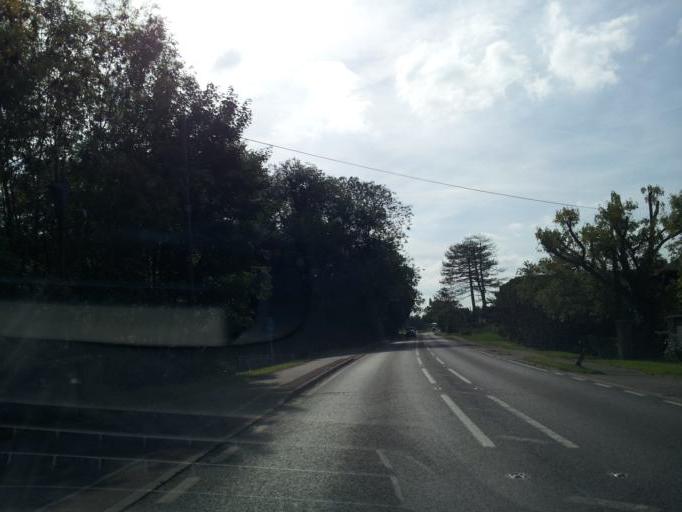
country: GB
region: England
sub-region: Cambridgeshire
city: Waterbeach
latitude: 52.2675
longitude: 0.1804
